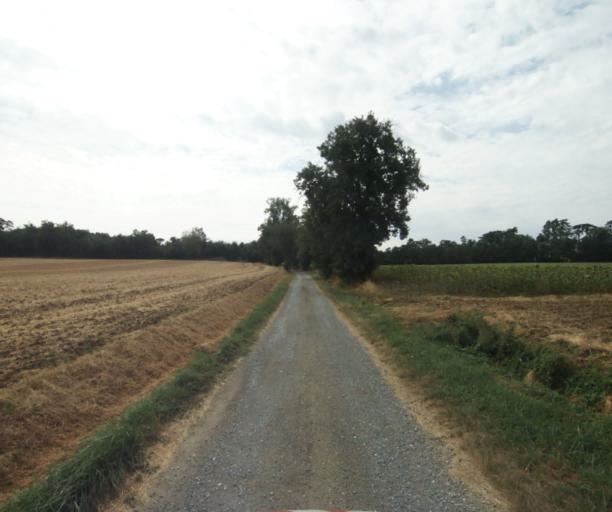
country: FR
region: Midi-Pyrenees
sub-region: Departement de la Haute-Garonne
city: Revel
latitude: 43.4466
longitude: 1.9628
